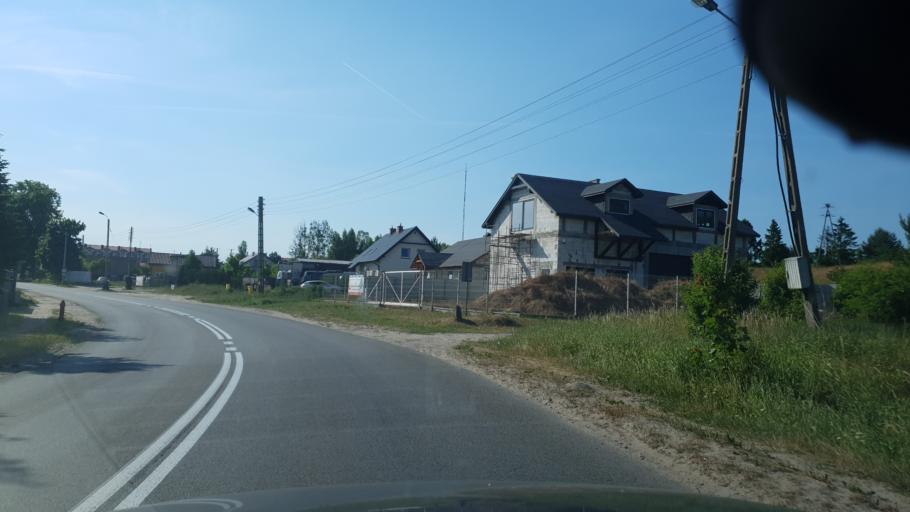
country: PL
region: Pomeranian Voivodeship
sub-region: Powiat kartuski
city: Chwaszczyno
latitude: 54.4414
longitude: 18.4552
